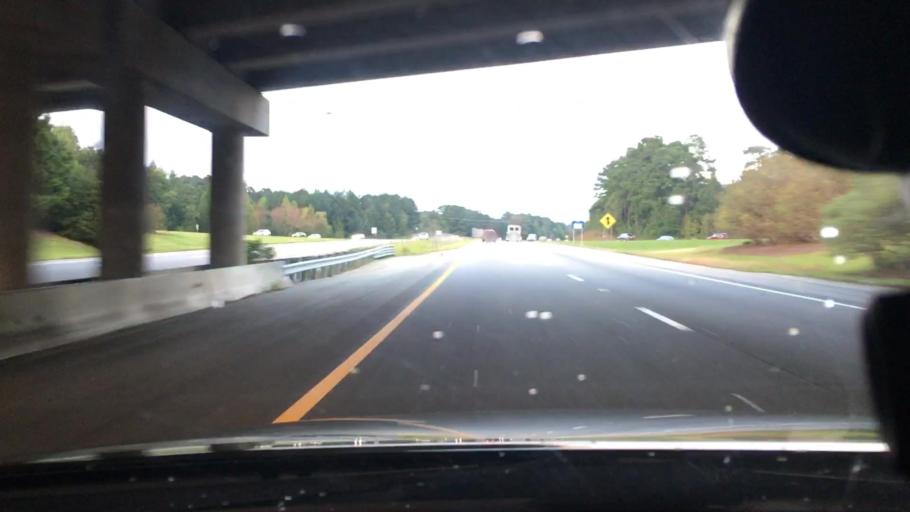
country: US
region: North Carolina
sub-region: Wake County
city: Apex
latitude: 35.7144
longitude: -78.8402
